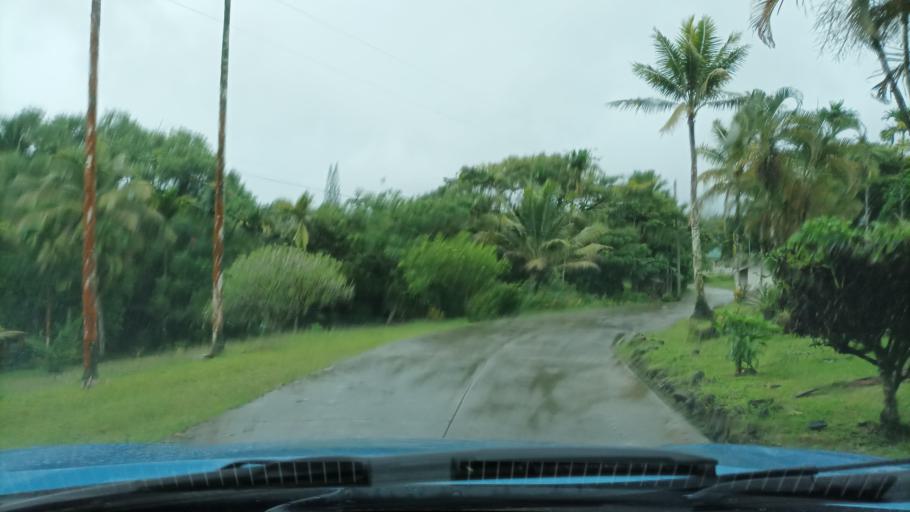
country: FM
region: Pohnpei
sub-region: Kolonia Municipality
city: Kolonia
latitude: 6.9572
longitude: 158.2117
